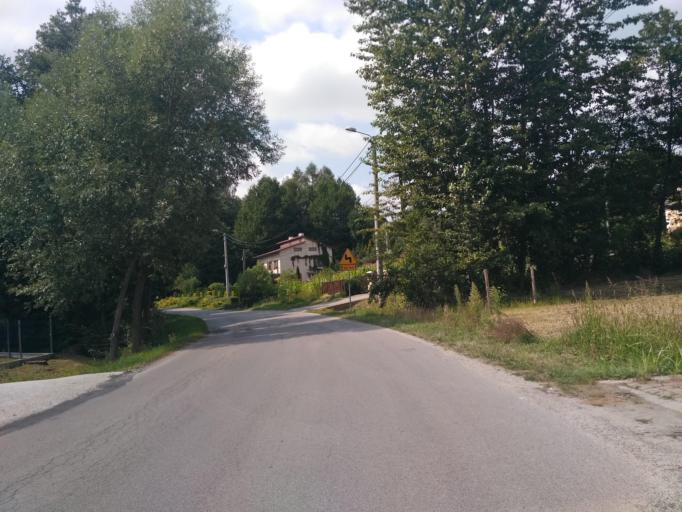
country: PL
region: Subcarpathian Voivodeship
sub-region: Powiat lancucki
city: Kraczkowa
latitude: 50.0231
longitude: 22.1844
